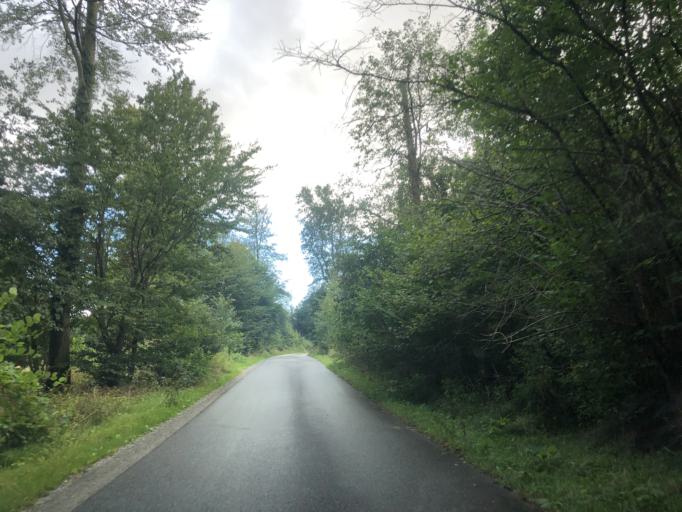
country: DK
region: South Denmark
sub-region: Vejle Kommune
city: Borkop
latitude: 55.6817
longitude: 9.6014
